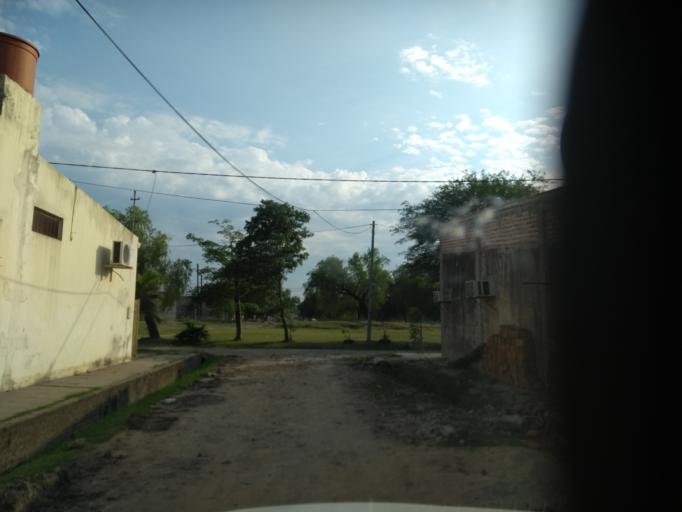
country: AR
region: Chaco
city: Resistencia
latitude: -27.4706
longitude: -58.9740
